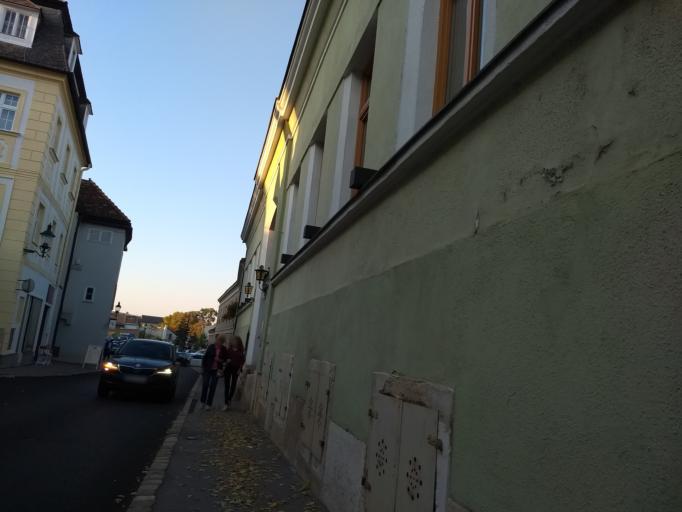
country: AT
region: Lower Austria
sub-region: Politischer Bezirk Modling
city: Perchtoldsdorf
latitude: 48.1211
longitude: 16.2642
